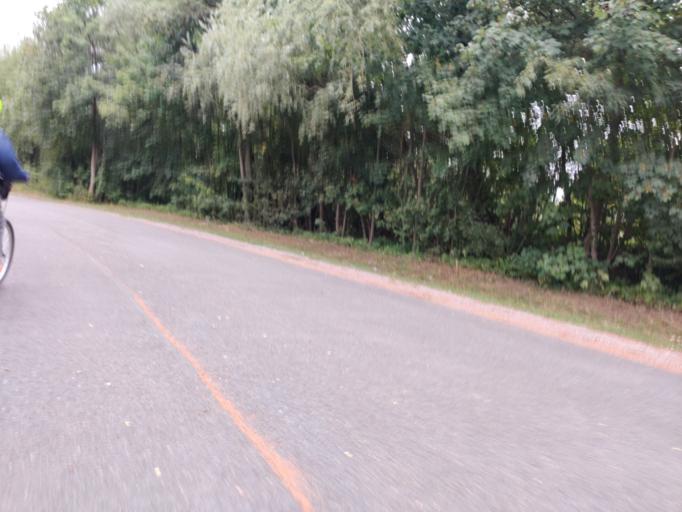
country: DE
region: North Rhine-Westphalia
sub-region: Regierungsbezirk Detmold
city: Hoexter
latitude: 51.7770
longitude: 9.4016
